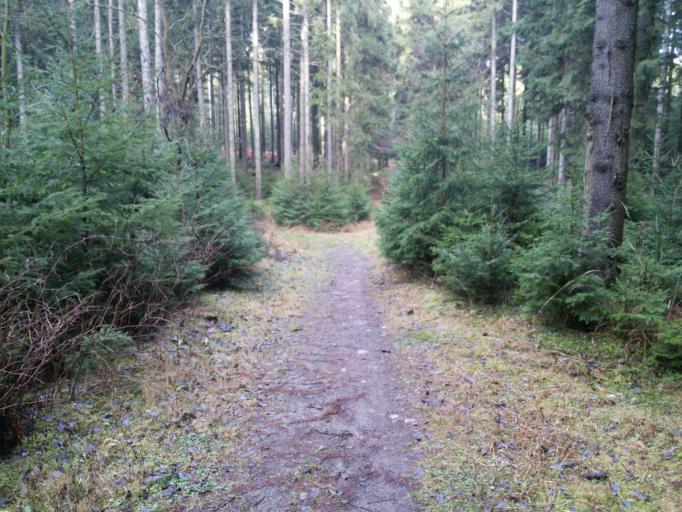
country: CZ
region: Vysocina
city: Zd'ar nad Sazavou Druhy
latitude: 49.5919
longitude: 15.9129
